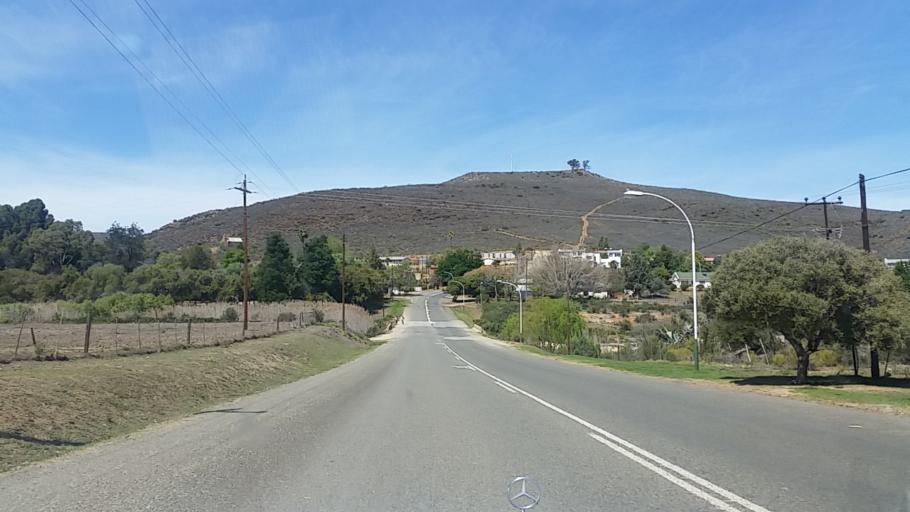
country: ZA
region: Western Cape
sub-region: Eden District Municipality
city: Knysna
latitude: -33.6528
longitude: 23.1348
